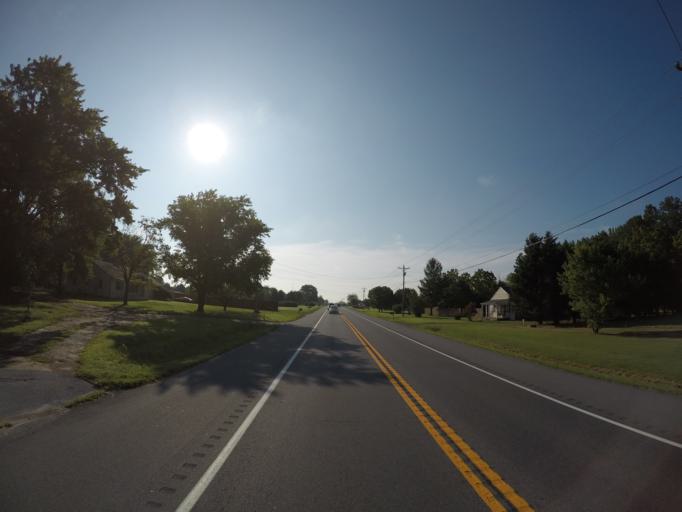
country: US
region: Delaware
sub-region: Sussex County
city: Bridgeville
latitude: 38.7056
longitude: -75.5139
